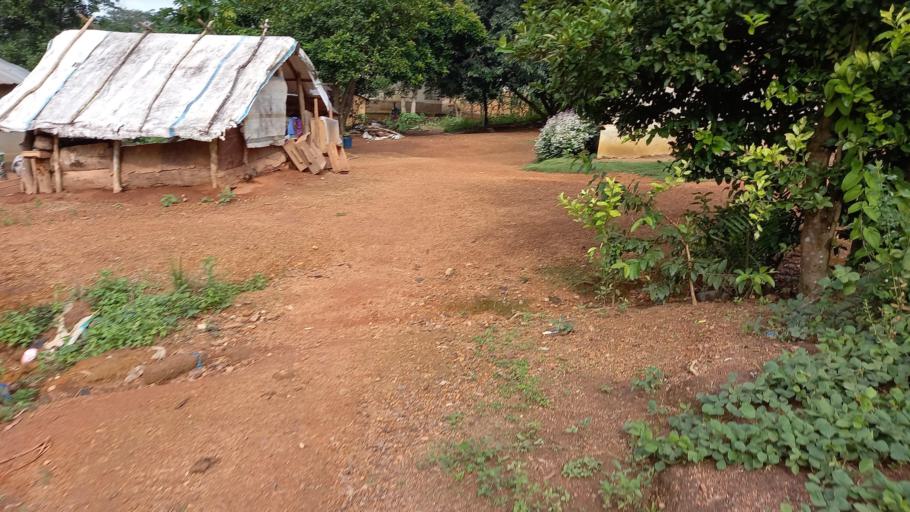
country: SL
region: Eastern Province
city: Kailahun
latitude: 8.2817
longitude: -10.5764
